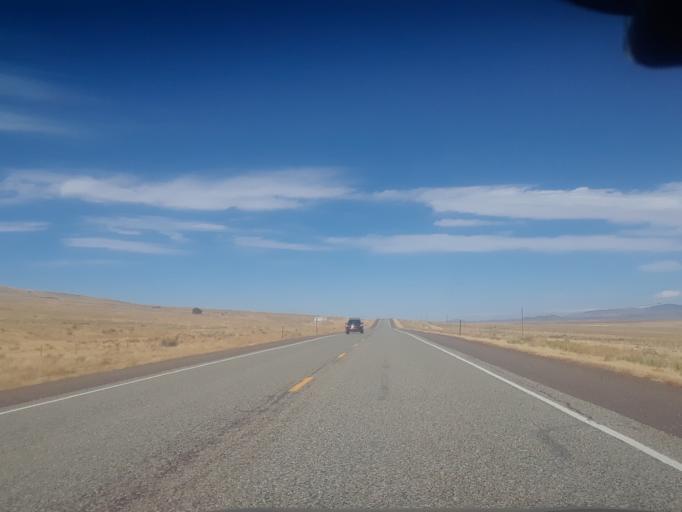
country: US
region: Colorado
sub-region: Conejos County
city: Conejos
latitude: 36.8490
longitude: -105.9722
